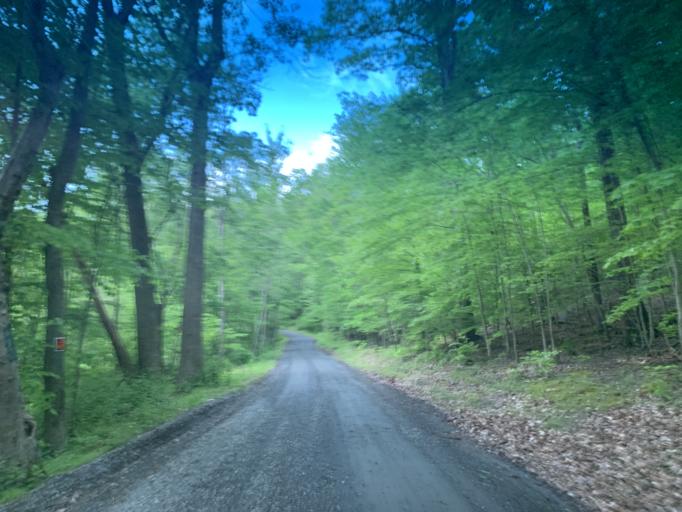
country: US
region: Pennsylvania
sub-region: York County
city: Susquehanna Trails
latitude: 39.6792
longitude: -76.2780
